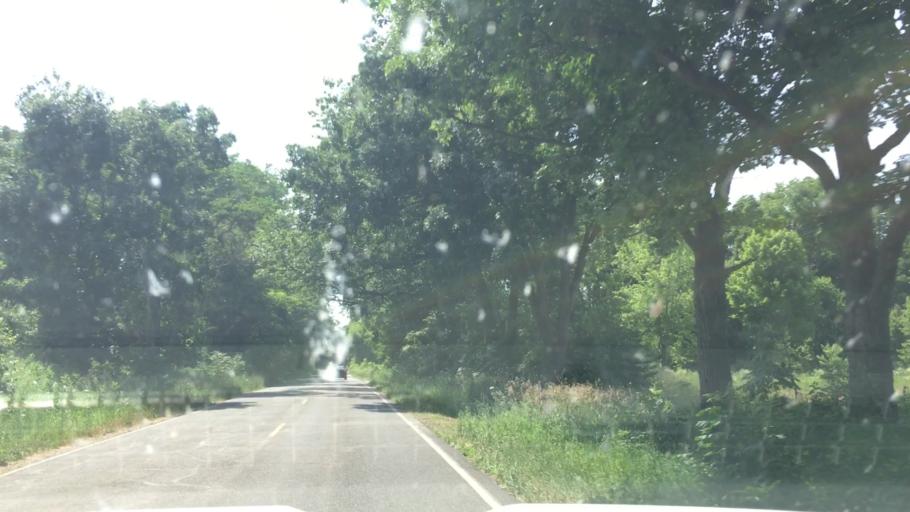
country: US
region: Michigan
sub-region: Kalamazoo County
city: Comstock Northwest
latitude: 42.4287
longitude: -85.5173
